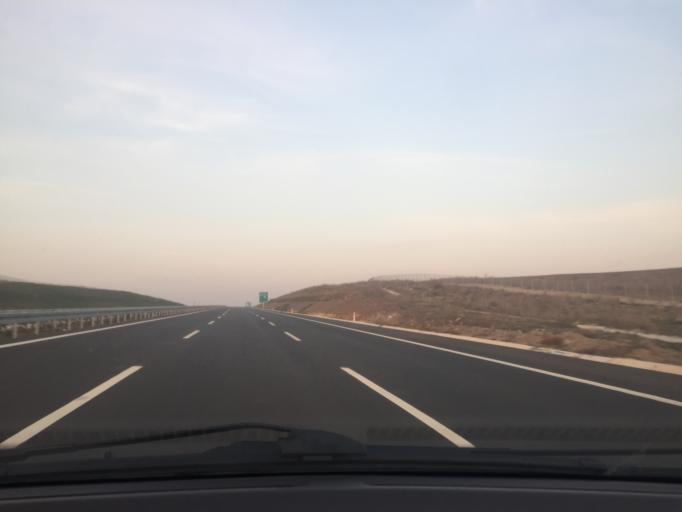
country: TR
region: Bursa
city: Mahmudiye
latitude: 40.2703
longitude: 28.6240
